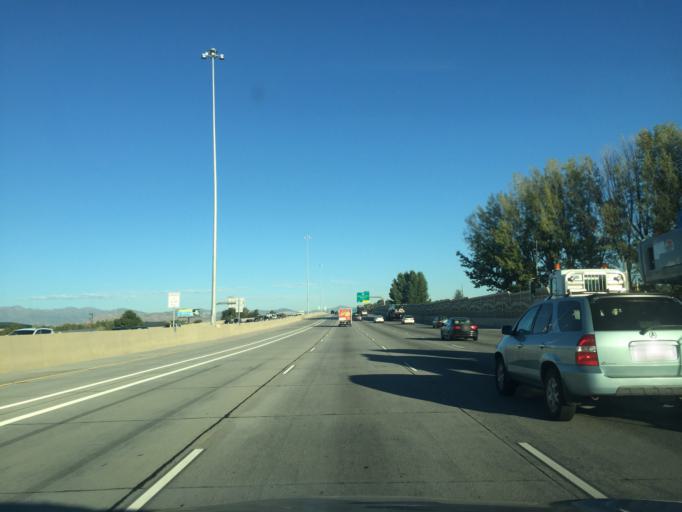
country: US
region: Utah
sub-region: Utah County
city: American Fork
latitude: 40.3645
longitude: -111.7914
